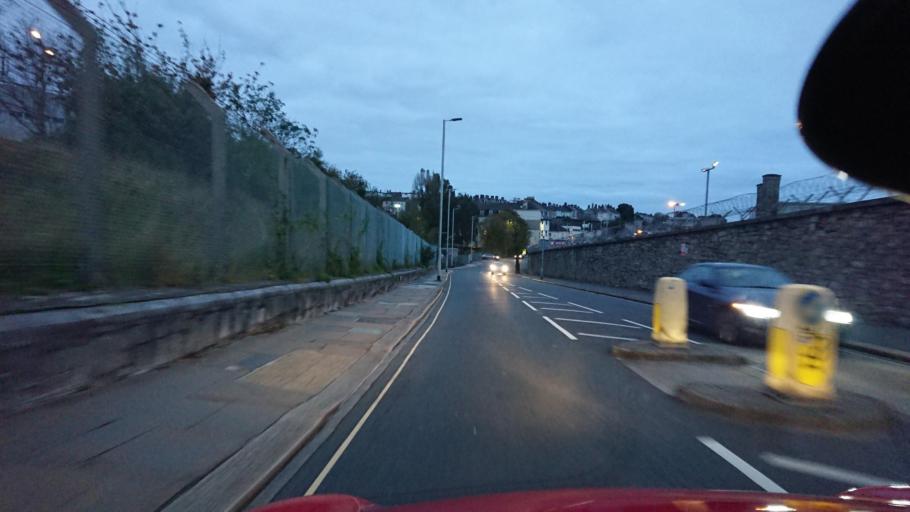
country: GB
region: England
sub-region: Cornwall
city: Torpoint
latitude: 50.3854
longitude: -4.1819
